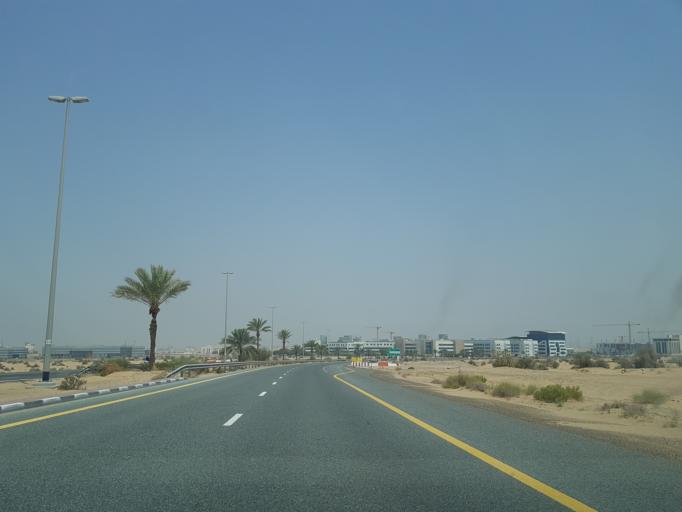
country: AE
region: Ash Shariqah
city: Sharjah
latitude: 25.1182
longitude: 55.4286
